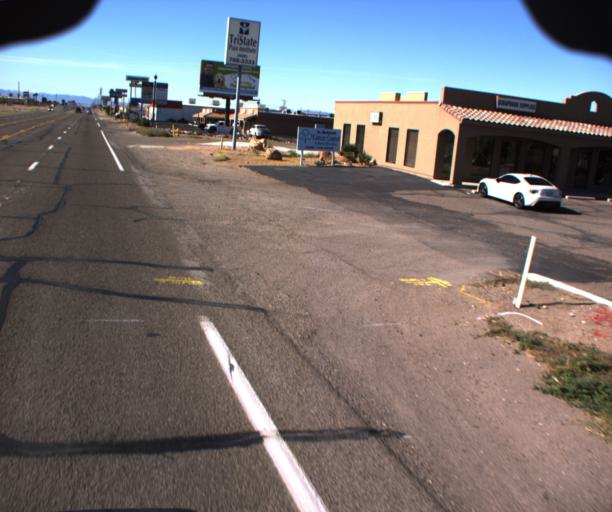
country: US
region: Arizona
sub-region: Mohave County
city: Mohave Valley
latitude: 35.0043
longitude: -114.5981
